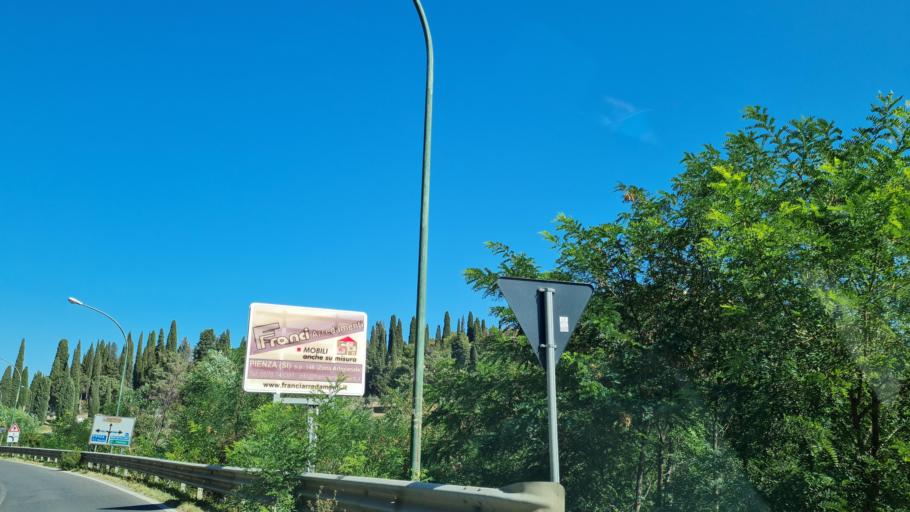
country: IT
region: Tuscany
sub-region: Provincia di Siena
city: Montepulciano
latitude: 43.0855
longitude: 11.7777
